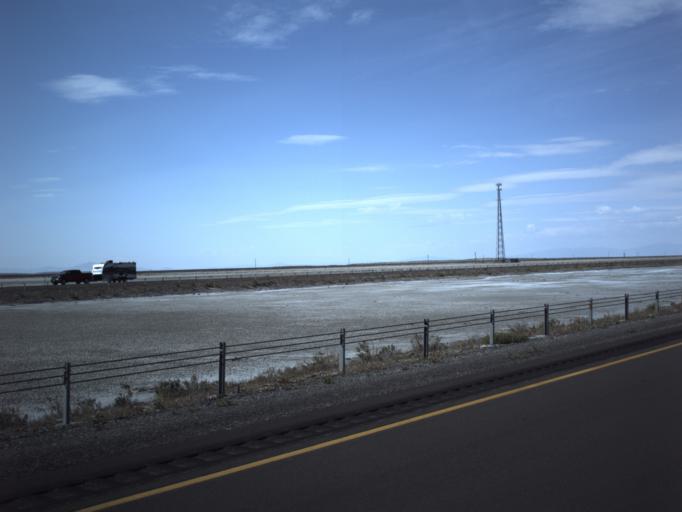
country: US
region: Utah
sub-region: Tooele County
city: Wendover
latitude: 40.7284
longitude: -113.3229
